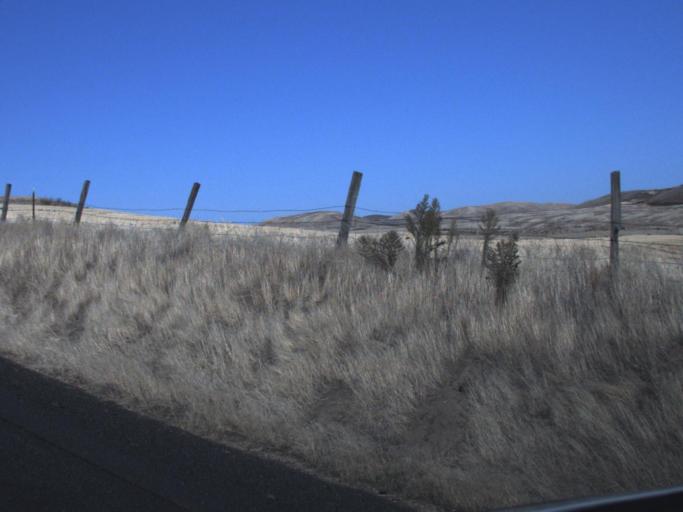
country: US
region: Washington
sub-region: Adams County
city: Ritzville
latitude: 46.7983
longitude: -118.2992
